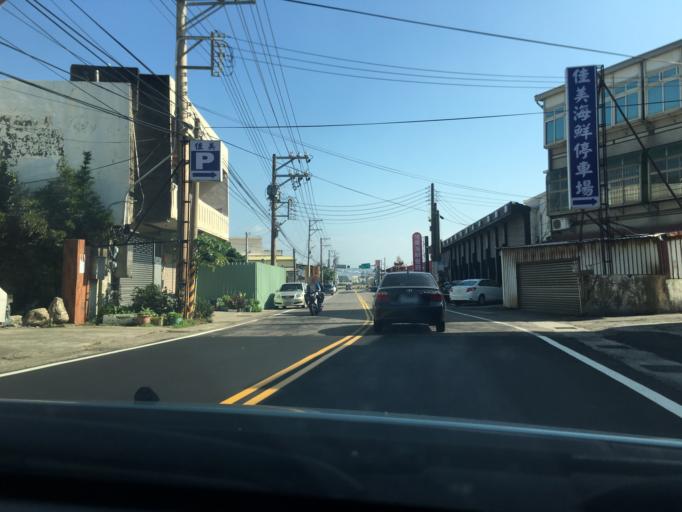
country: TW
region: Taiwan
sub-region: Hsinchu
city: Hsinchu
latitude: 24.8062
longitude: 120.9217
